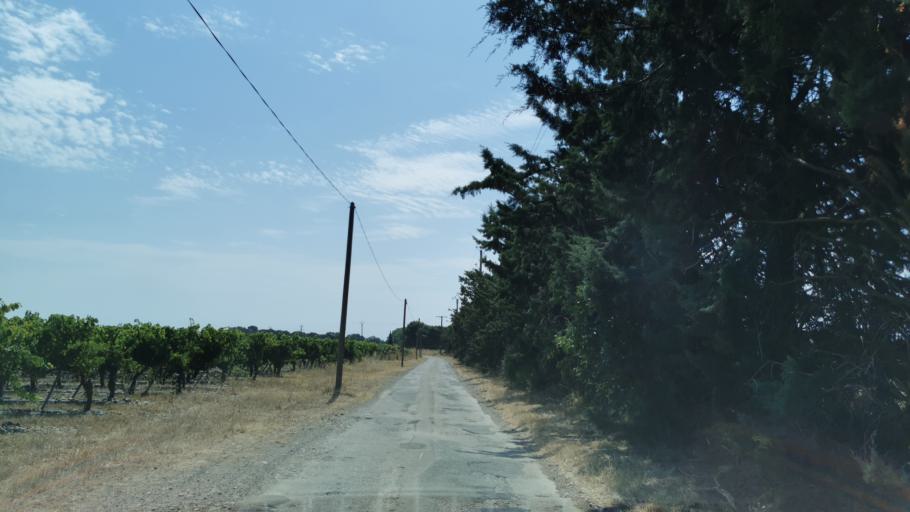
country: FR
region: Languedoc-Roussillon
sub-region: Departement de l'Aude
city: Argeliers
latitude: 43.2903
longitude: 2.8908
